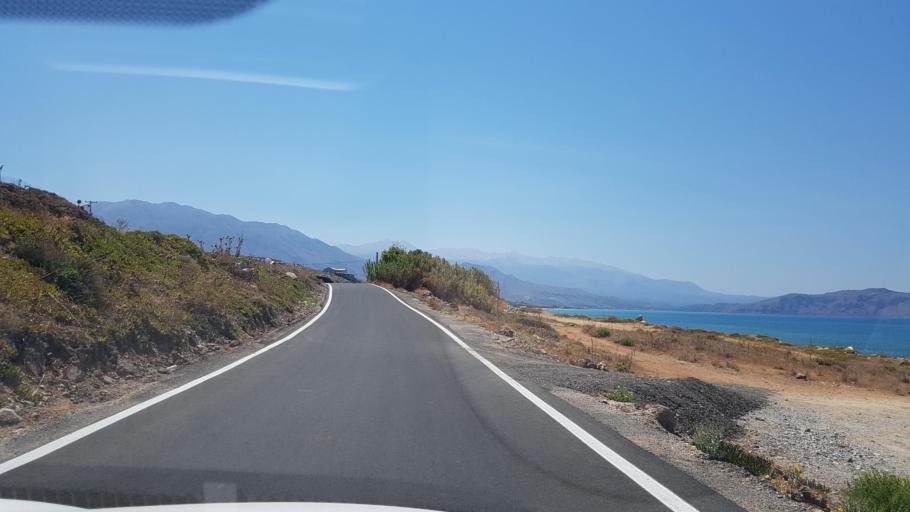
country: GR
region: Crete
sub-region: Nomos Rethymnis
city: Atsipopoulon
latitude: 35.3520
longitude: 24.3609
